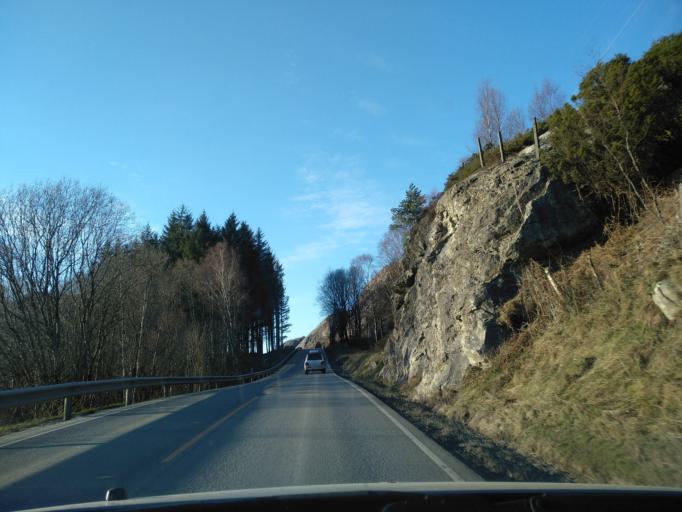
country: NO
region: Rogaland
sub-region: Tysvaer
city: Aksdal
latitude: 59.4576
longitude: 5.4928
